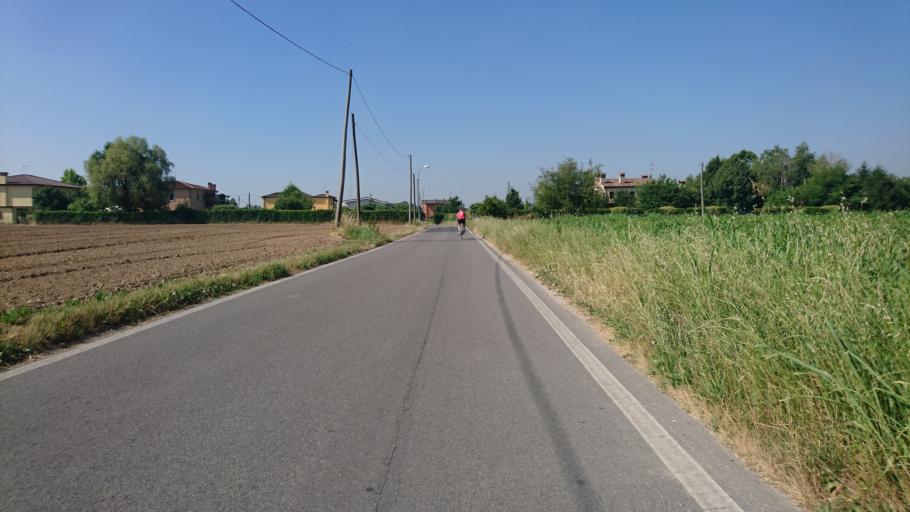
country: IT
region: Veneto
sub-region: Provincia di Padova
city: Tencarola
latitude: 45.3703
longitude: 11.8099
